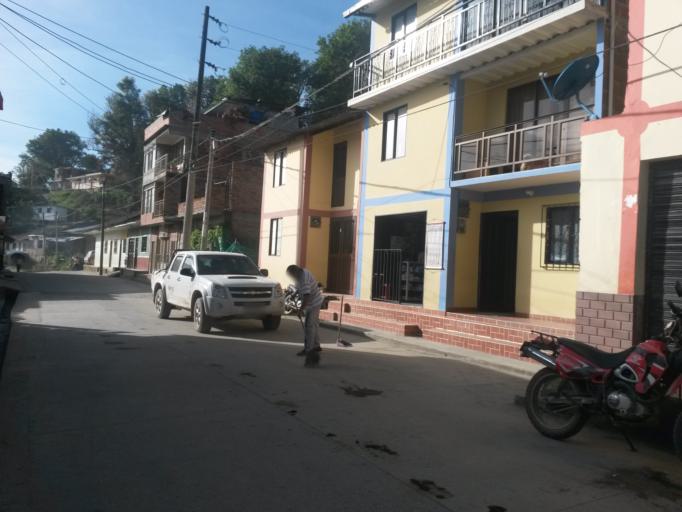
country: CO
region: Cauca
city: Inza
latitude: 2.5494
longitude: -76.0645
